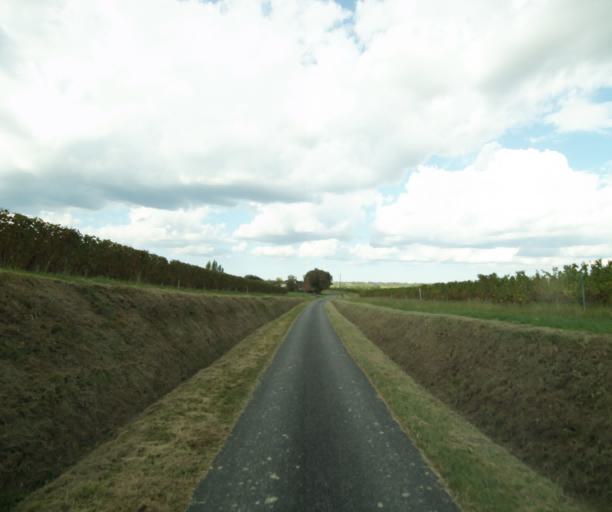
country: FR
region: Midi-Pyrenees
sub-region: Departement du Gers
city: Cazaubon
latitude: 43.8919
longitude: -0.0543
